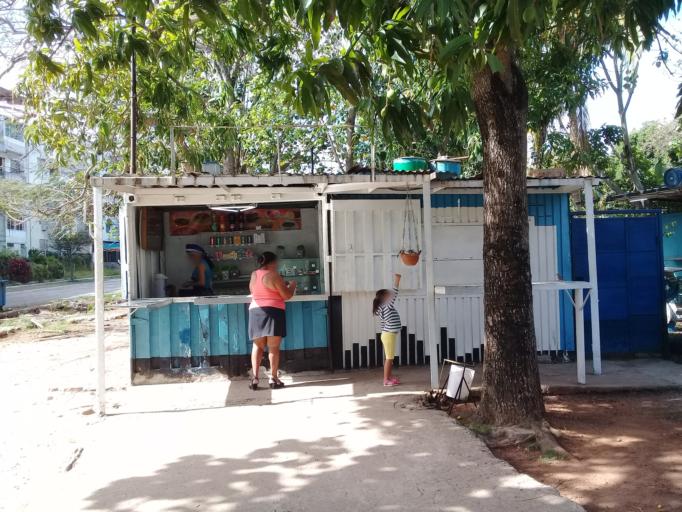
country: CU
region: La Habana
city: Alamar
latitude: 23.1553
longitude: -82.2810
